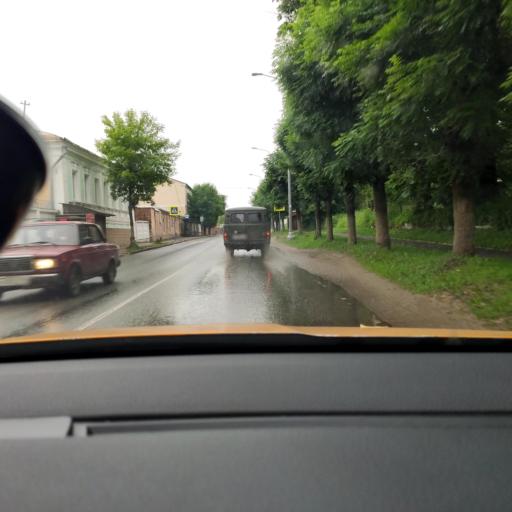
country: RU
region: Moskovskaya
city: Serpukhov
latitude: 54.9177
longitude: 37.3900
